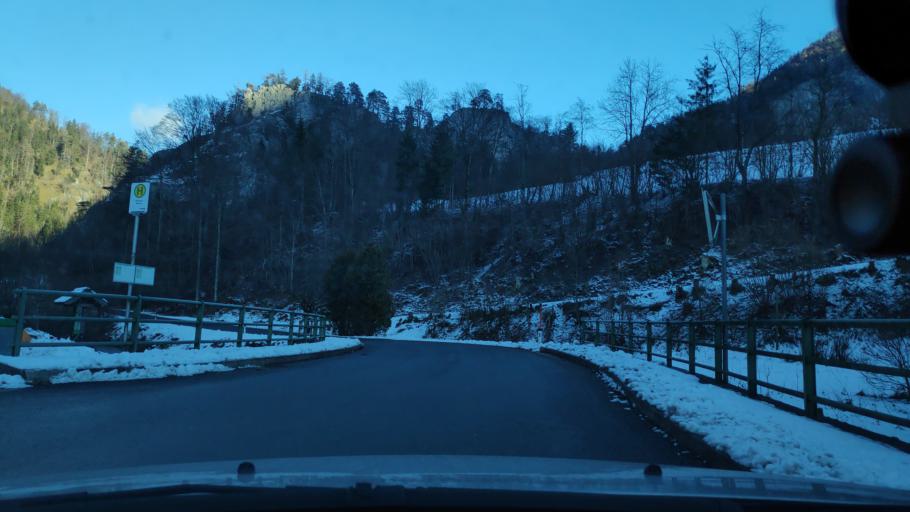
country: AT
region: Lower Austria
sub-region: Politischer Bezirk Neunkirchen
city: Schwarzau im Gebirge
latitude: 47.7666
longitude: 15.7071
